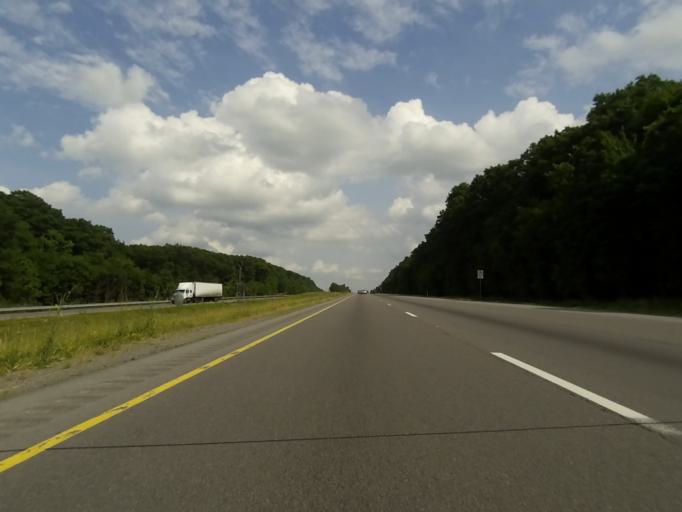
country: US
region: Pennsylvania
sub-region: Clearfield County
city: Clearfield
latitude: 41.1047
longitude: -78.5337
